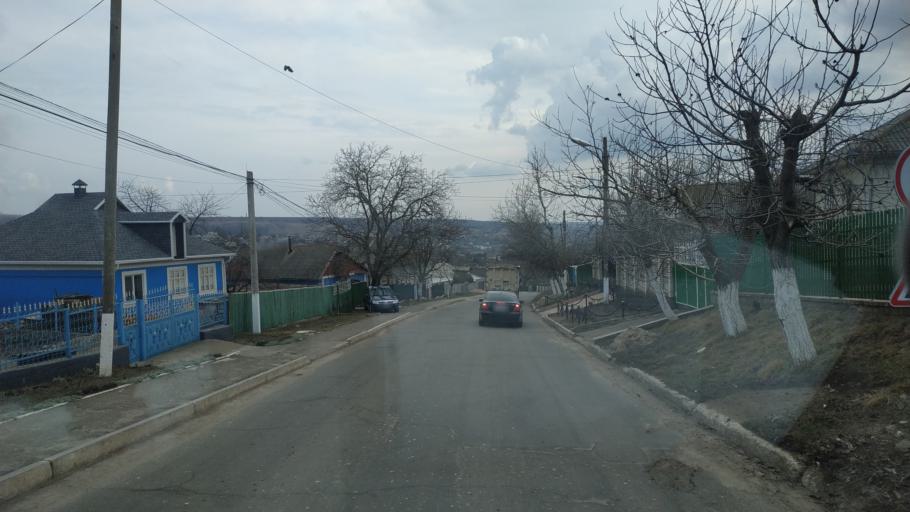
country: MD
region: Anenii Noi
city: Varnita
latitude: 46.8488
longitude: 29.3549
